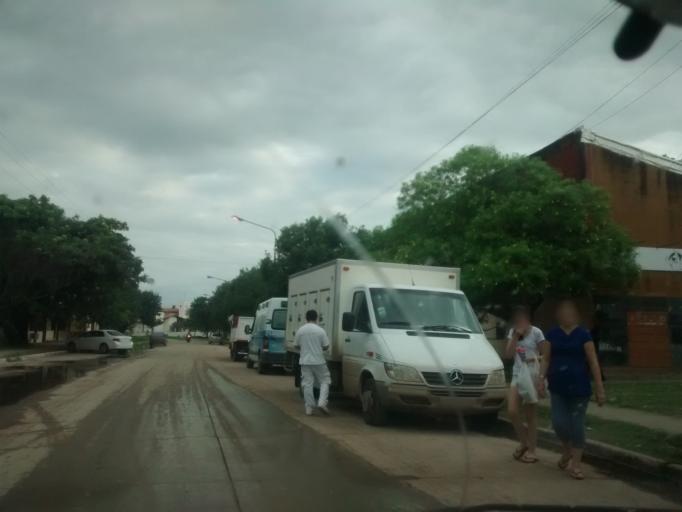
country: AR
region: Chaco
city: Fontana
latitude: -27.4420
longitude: -59.0166
